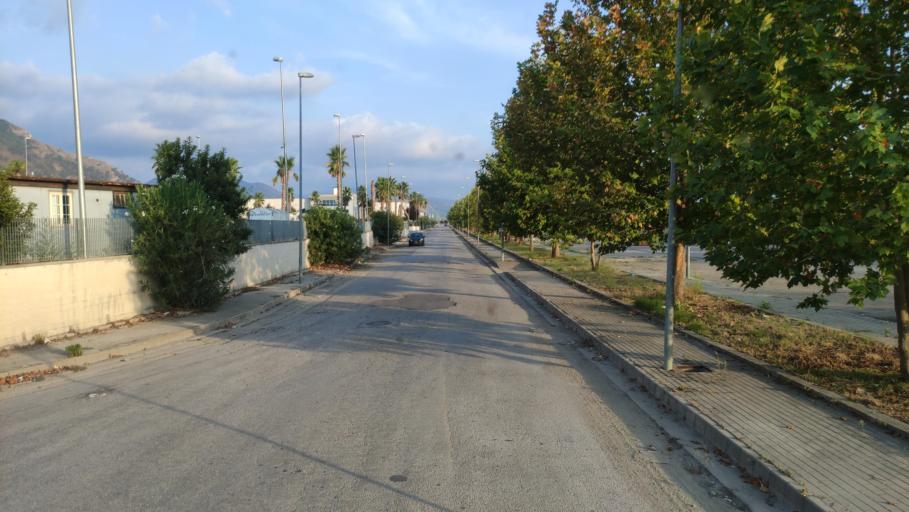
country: IT
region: Campania
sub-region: Provincia di Napoli
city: Striano
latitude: 40.8199
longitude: 14.5923
